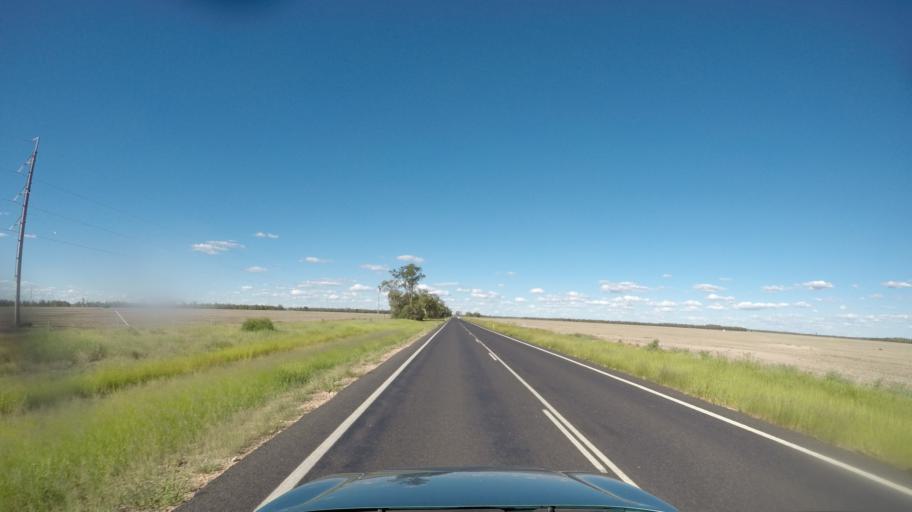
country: AU
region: Queensland
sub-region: Goondiwindi
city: Goondiwindi
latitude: -28.1481
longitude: 150.6844
